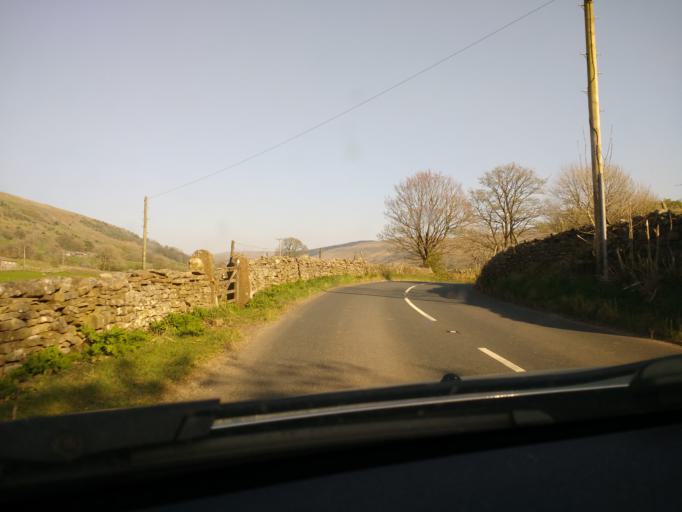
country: GB
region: England
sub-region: Cumbria
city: Sedbergh
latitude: 54.3090
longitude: -2.4253
